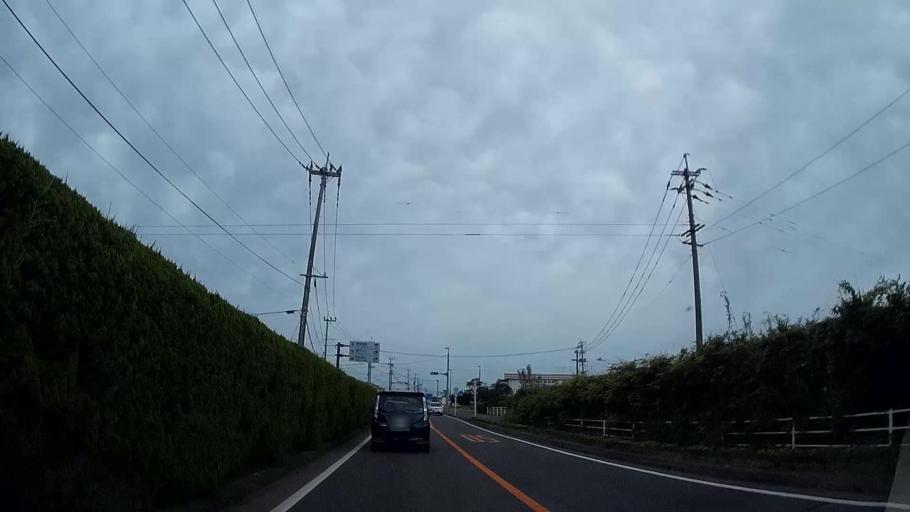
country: JP
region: Kumamoto
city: Kikuchi
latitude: 32.9716
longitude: 130.8100
